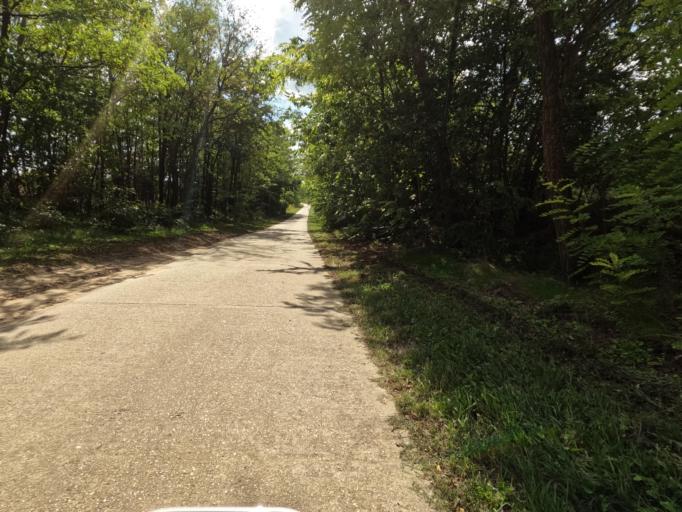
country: HU
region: Tolna
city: Tengelic
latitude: 46.5117
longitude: 18.6913
